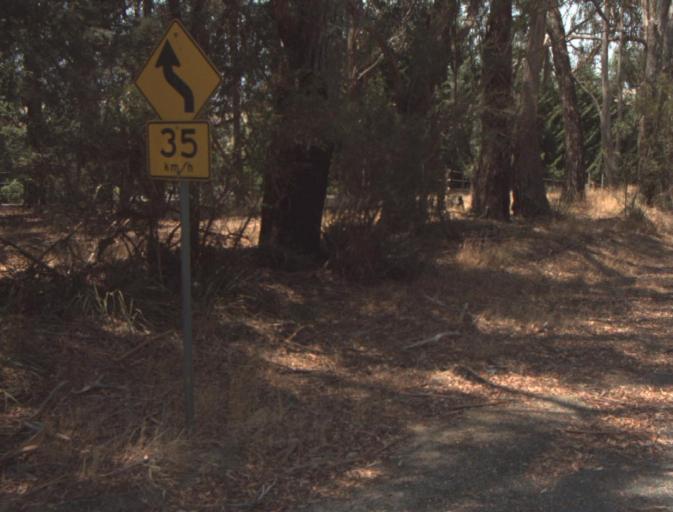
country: AU
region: Tasmania
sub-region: Launceston
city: Newstead
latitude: -41.4883
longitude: 147.1958
